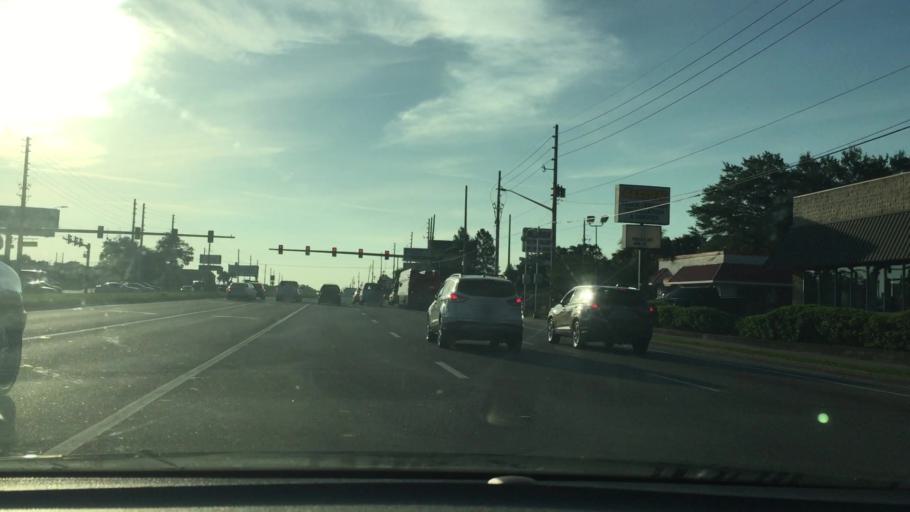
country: US
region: Florida
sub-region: Orange County
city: Pine Hills
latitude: 28.5524
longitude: -81.4486
